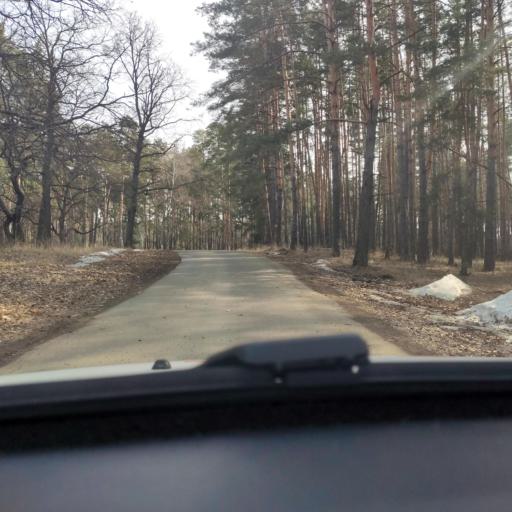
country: RU
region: Voronezj
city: Ramon'
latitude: 51.8910
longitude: 39.3637
